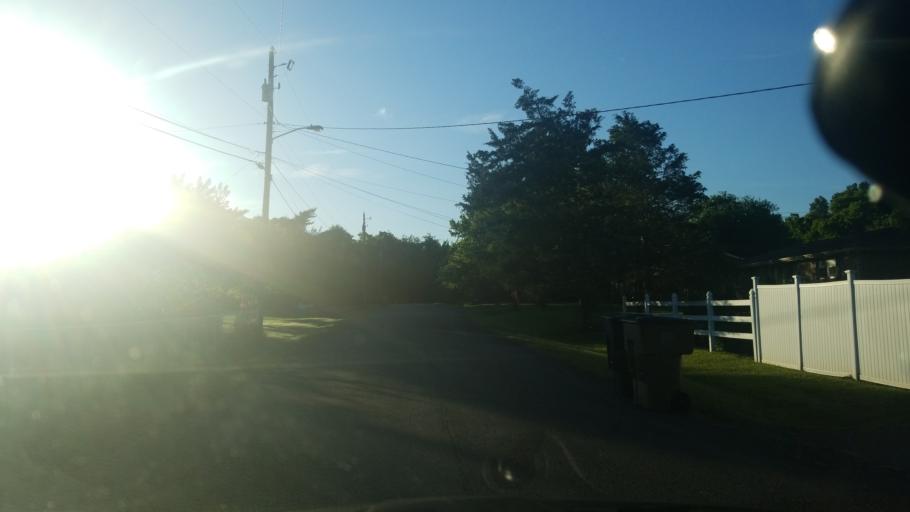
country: US
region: Tennessee
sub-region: Davidson County
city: Nashville
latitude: 36.2281
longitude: -86.7658
